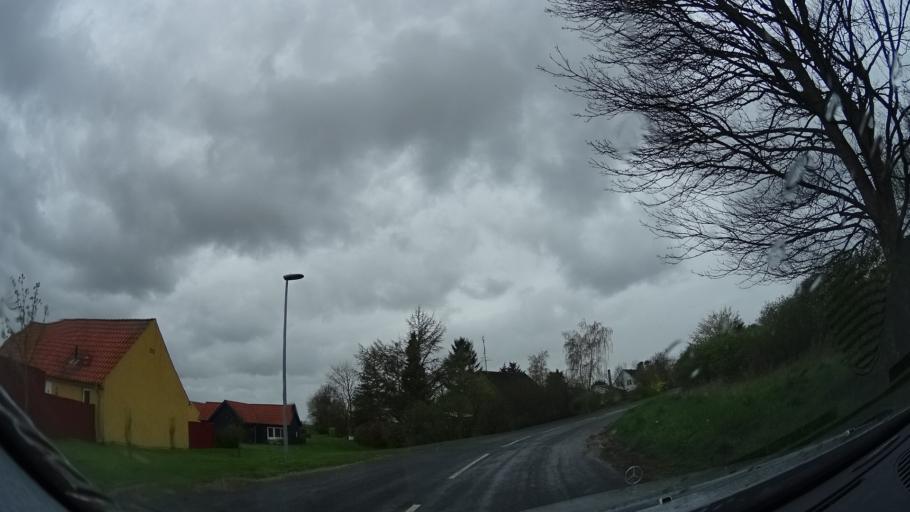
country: DK
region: Zealand
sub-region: Holbaek Kommune
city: Vipperod
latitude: 55.7046
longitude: 11.7755
